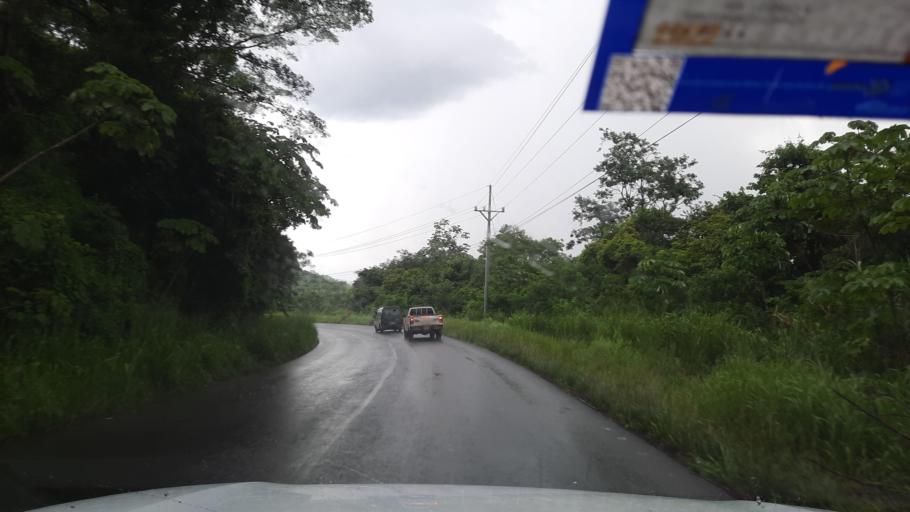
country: CR
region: Alajuela
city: San Rafael
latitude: 10.0333
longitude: -84.5586
